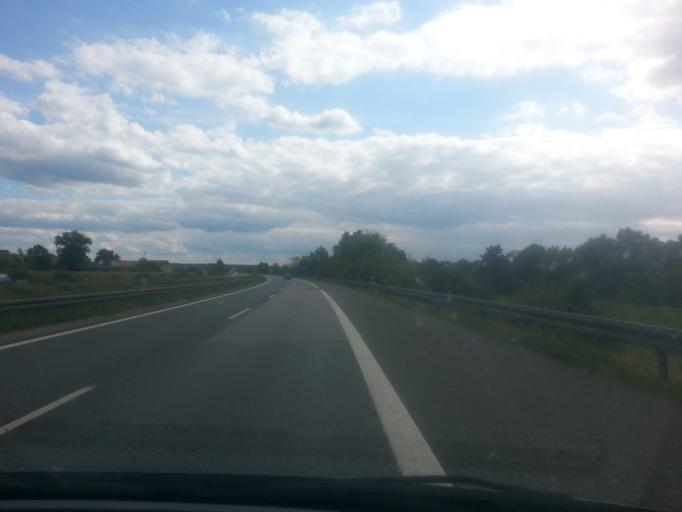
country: DE
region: Bavaria
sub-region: Upper Palatinate
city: Schwarzenfeld
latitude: 49.3851
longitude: 12.1479
